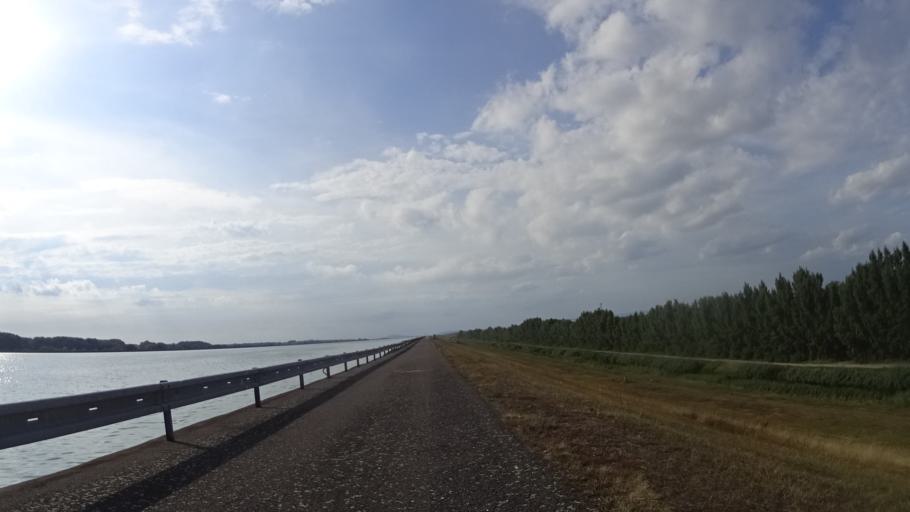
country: HU
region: Gyor-Moson-Sopron
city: Asvanyraro
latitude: 47.9384
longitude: 17.4577
